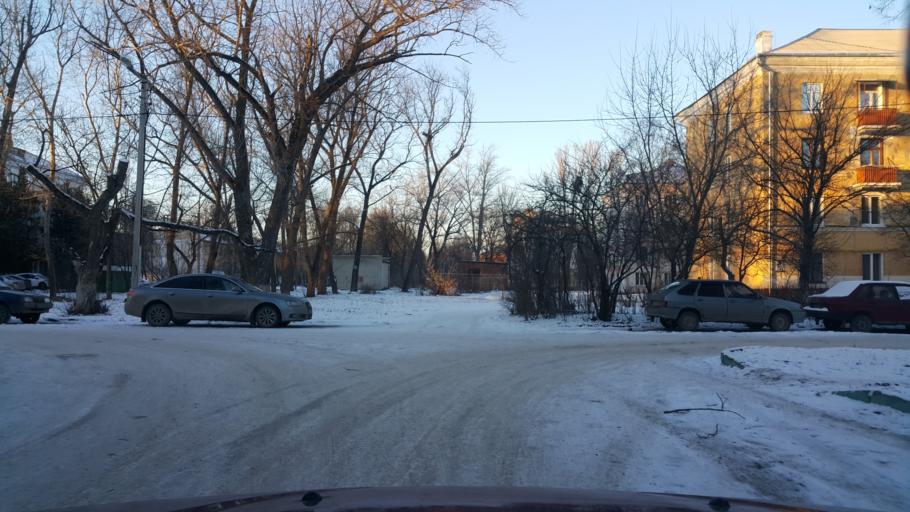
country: RU
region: Tambov
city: Pokrovo-Prigorodnoye
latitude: 52.7082
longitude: 41.3939
